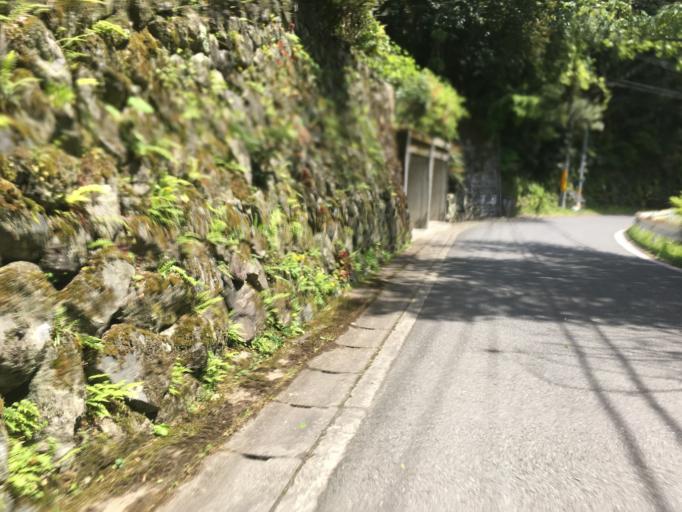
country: JP
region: Kyoto
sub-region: Kyoto-shi
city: Kamigyo-ku
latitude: 35.1126
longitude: 135.7227
